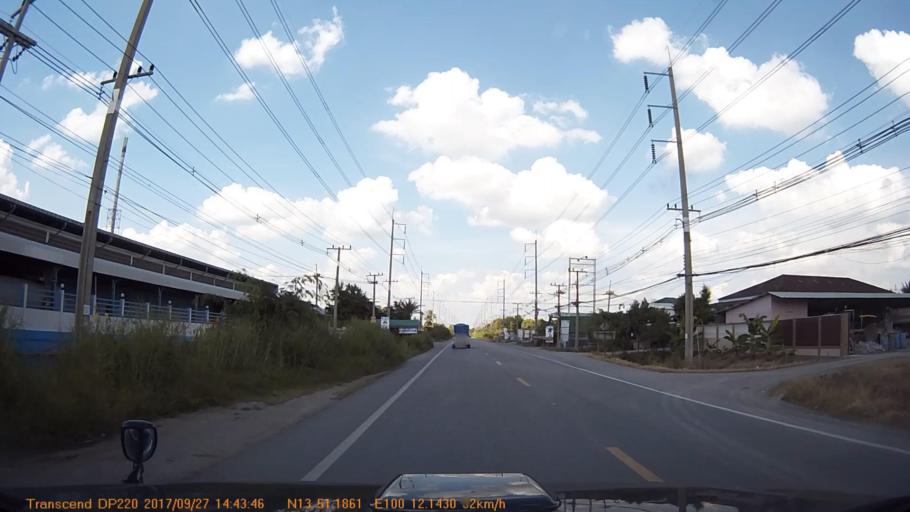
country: TH
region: Nakhon Pathom
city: Nakhon Chai Si
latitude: 13.8531
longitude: 100.2024
